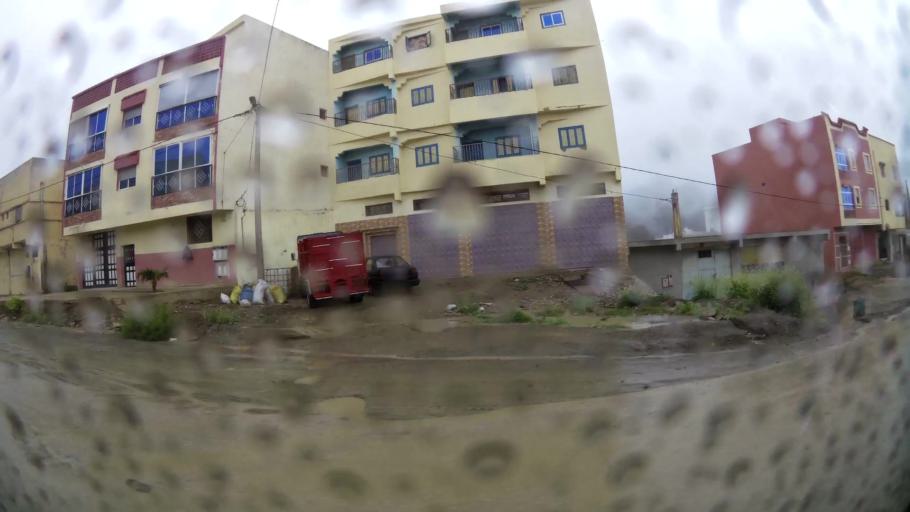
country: MA
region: Taza-Al Hoceima-Taounate
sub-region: Taza
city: Aknoul
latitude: 34.7652
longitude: -3.7937
